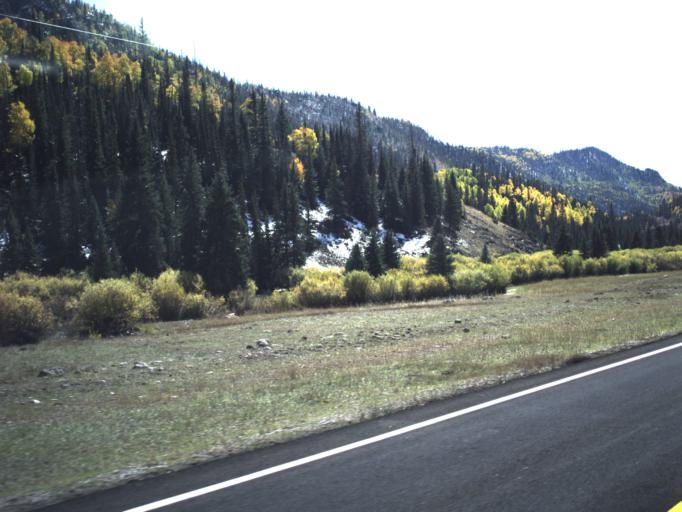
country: US
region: Utah
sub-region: Beaver County
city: Beaver
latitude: 38.2978
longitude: -112.4370
